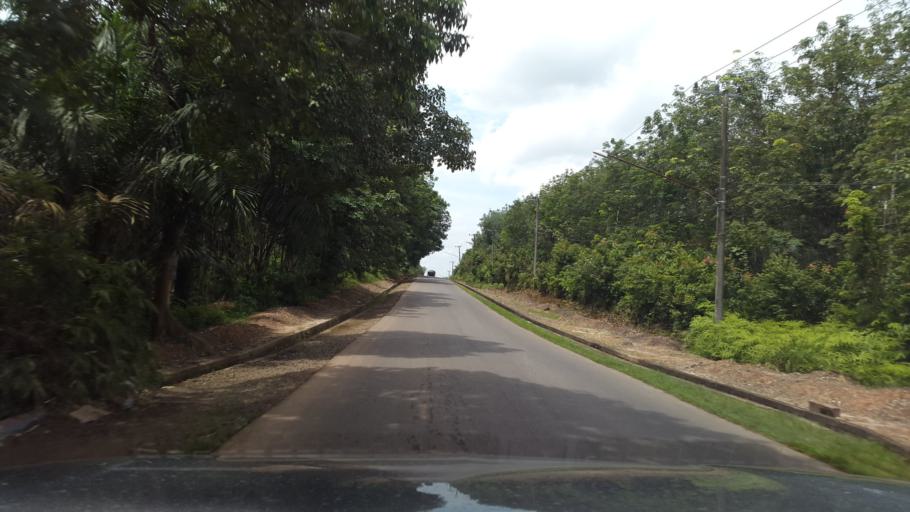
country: ID
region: South Sumatra
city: Gunungmegang Dalam
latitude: -3.3148
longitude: 103.8923
